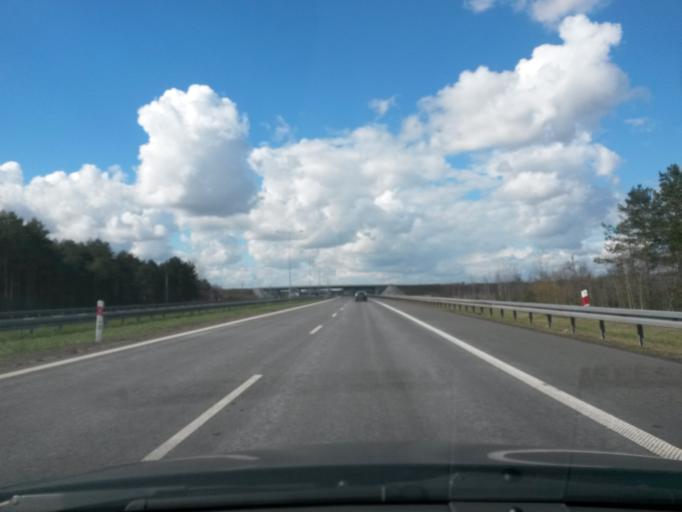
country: PL
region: Greater Poland Voivodeship
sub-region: Powiat kolski
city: Dabie
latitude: 52.0651
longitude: 18.8265
